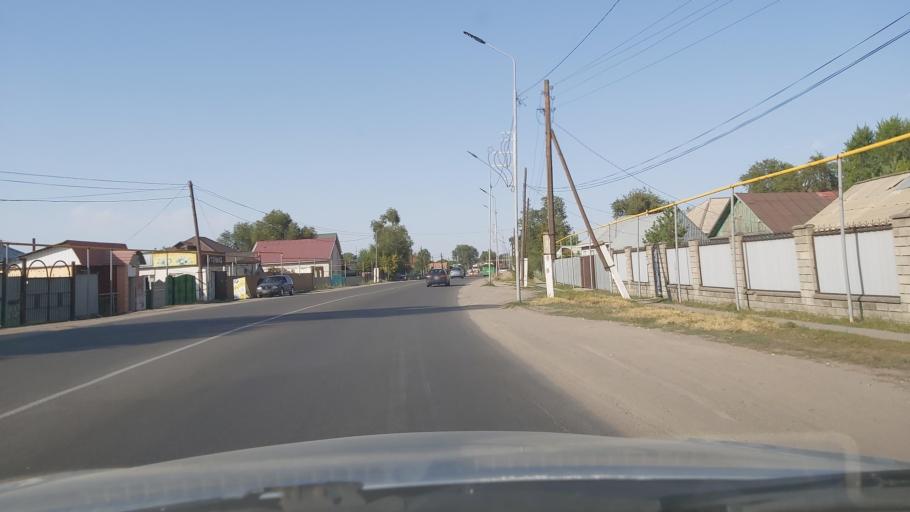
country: KZ
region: Almaty Oblysy
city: Energeticheskiy
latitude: 43.4904
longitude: 77.0343
